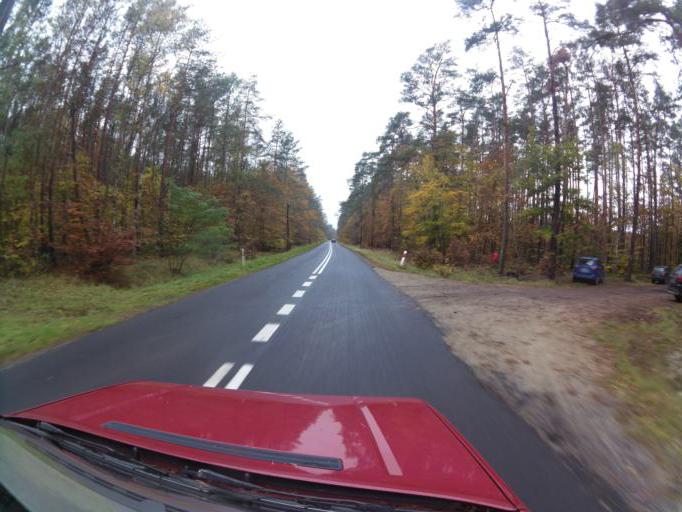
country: PL
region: West Pomeranian Voivodeship
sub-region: Powiat policki
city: Dobra
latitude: 53.5982
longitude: 14.3431
